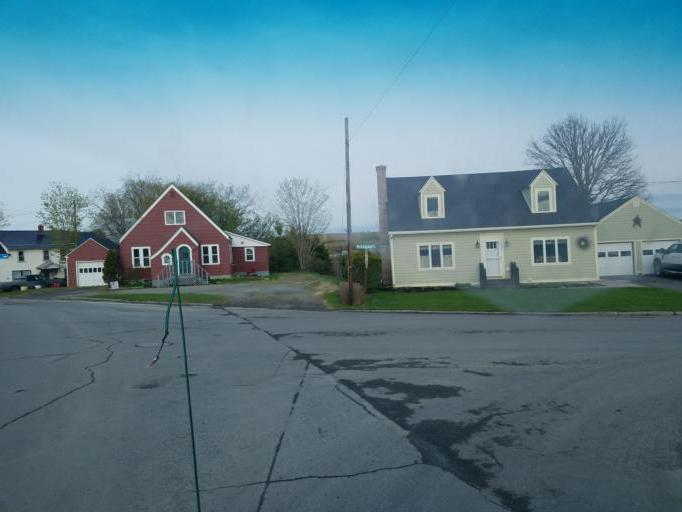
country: US
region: Maine
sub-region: Aroostook County
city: Caribou
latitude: 46.8605
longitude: -68.0054
